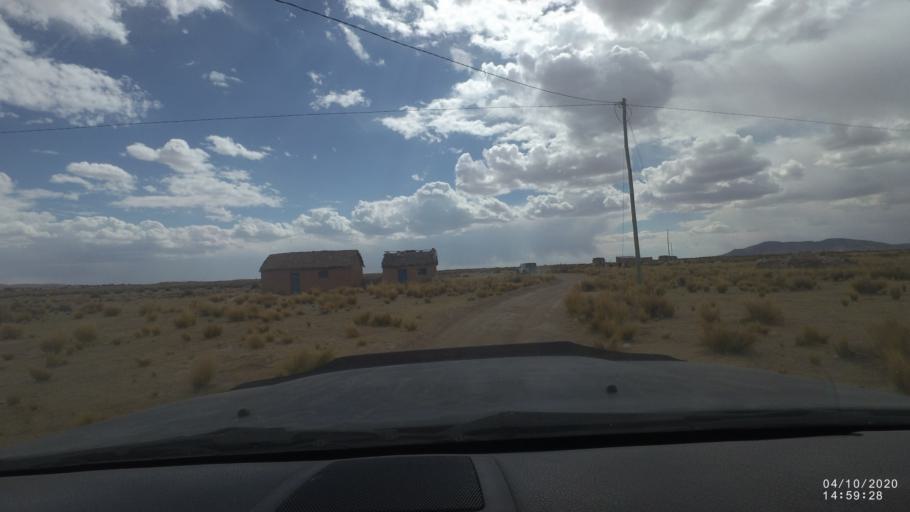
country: BO
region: Oruro
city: Poopo
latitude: -18.6863
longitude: -67.5227
